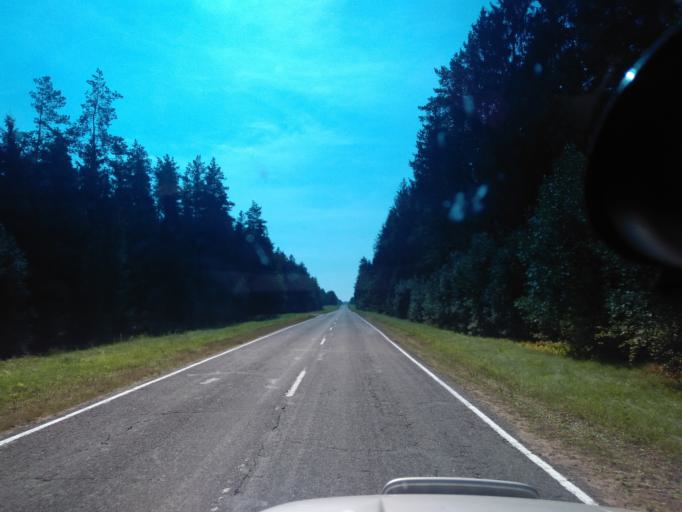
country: BY
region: Minsk
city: Uzda
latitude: 53.3307
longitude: 27.2307
